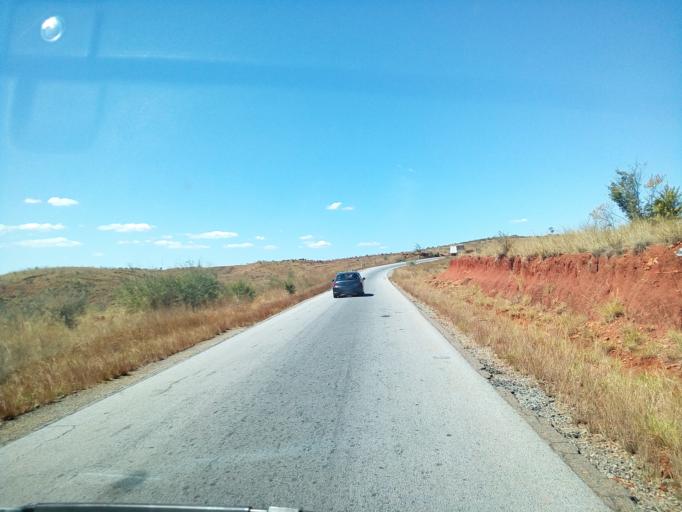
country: MG
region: Betsiboka
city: Maevatanana
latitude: -17.1382
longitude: 46.8168
